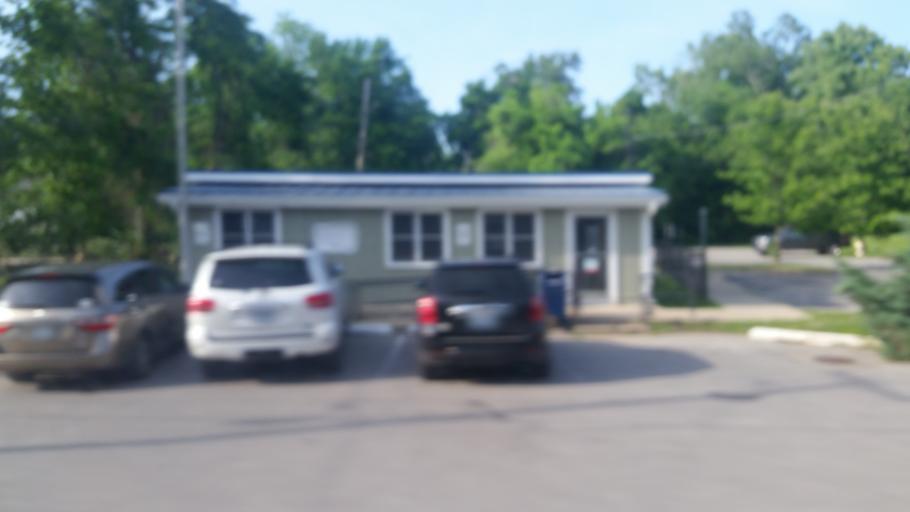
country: US
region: Kentucky
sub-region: Jefferson County
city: Prospect
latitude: 38.3276
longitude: -85.6346
